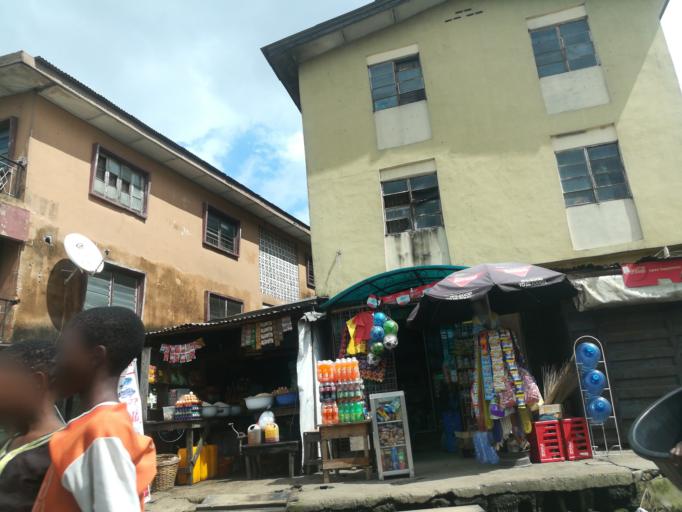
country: NG
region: Lagos
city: Mushin
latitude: 6.5380
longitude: 3.3615
